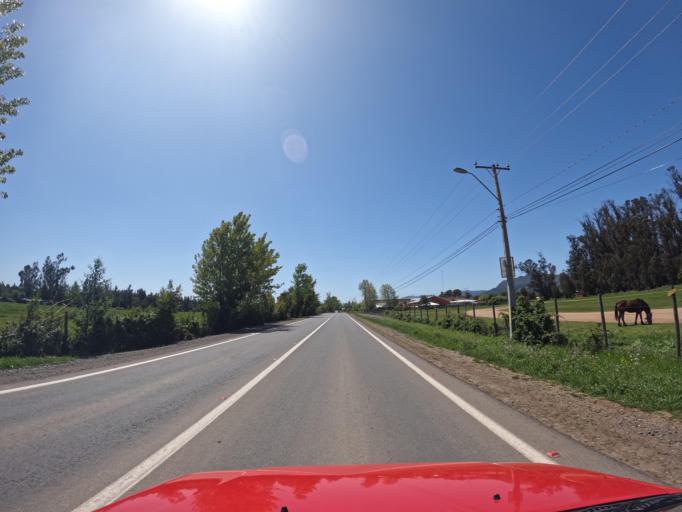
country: CL
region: Maule
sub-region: Provincia de Linares
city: Colbun
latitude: -35.7600
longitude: -71.4200
